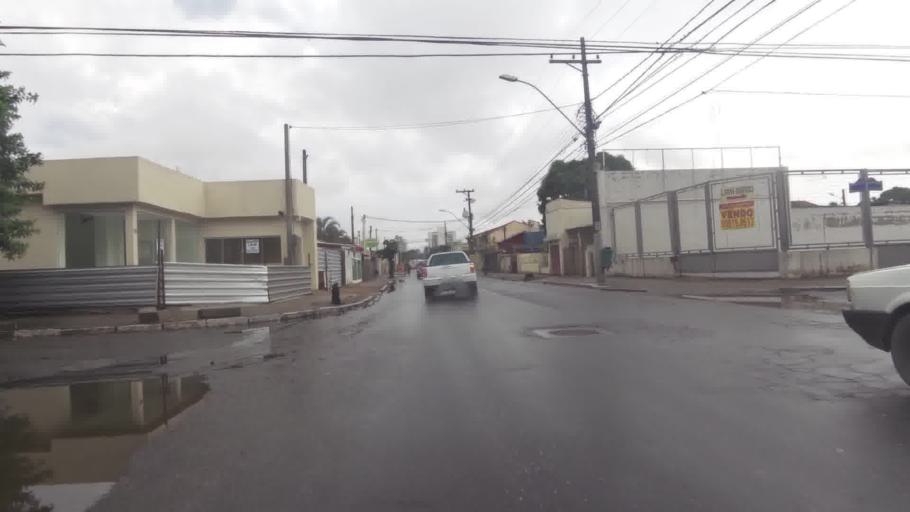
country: BR
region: Rio de Janeiro
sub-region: Campos Dos Goytacazes
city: Campos
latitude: -21.7463
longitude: -41.3356
